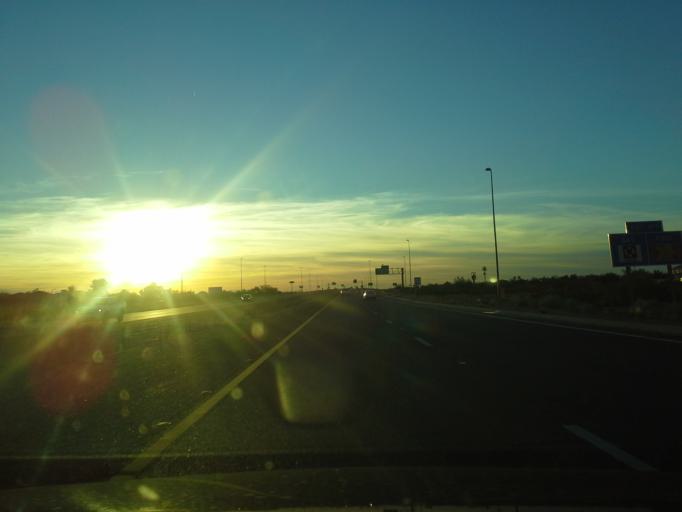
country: US
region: Arizona
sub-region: Pinal County
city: Apache Junction
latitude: 33.3867
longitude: -111.5201
